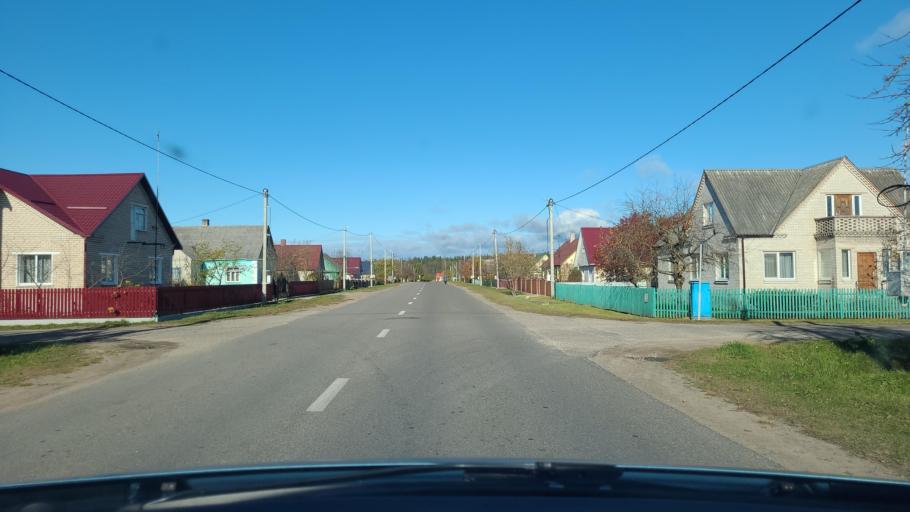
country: BY
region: Grodnenskaya
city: Astravyets
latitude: 54.6148
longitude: 25.9464
